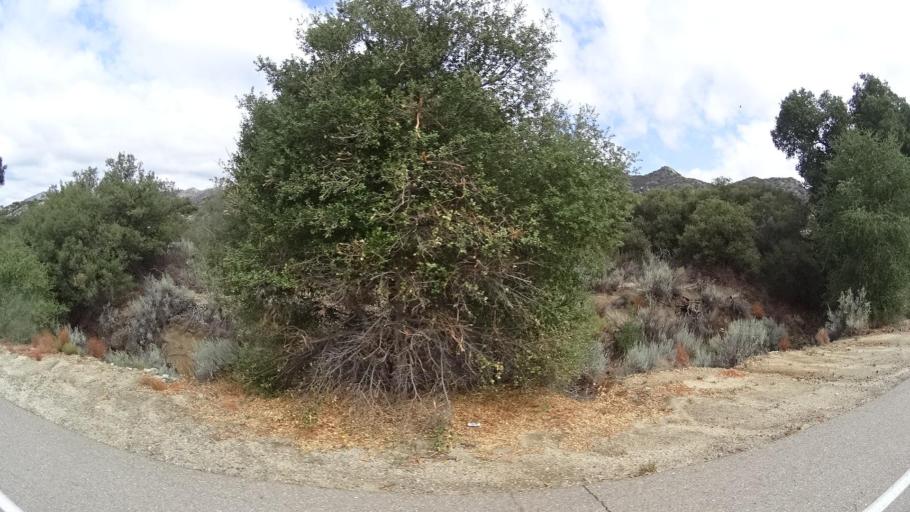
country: US
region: California
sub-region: San Diego County
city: Pine Valley
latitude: 32.7276
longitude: -116.4807
